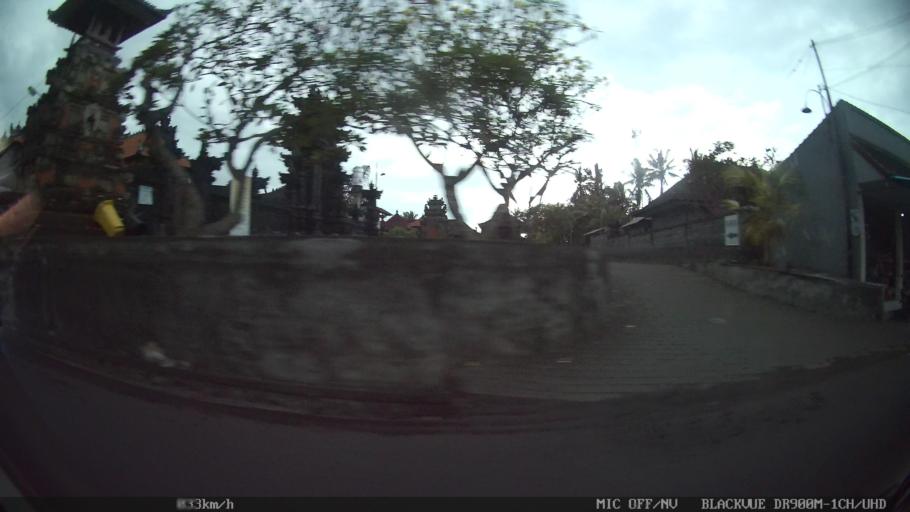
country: ID
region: Bali
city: Banjar Pasekan
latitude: -8.6211
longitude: 115.2982
